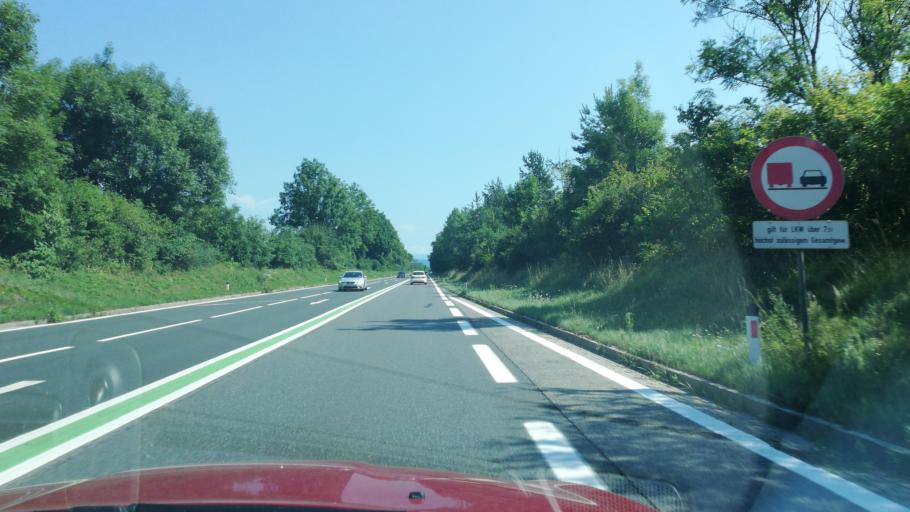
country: AT
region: Carinthia
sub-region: Politischer Bezirk Klagenfurt Land
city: Maria Saal
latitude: 46.6714
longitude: 14.3222
